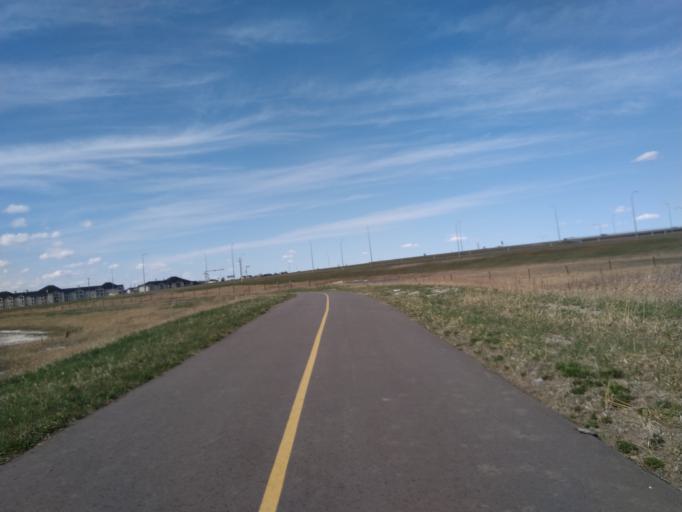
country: CA
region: Alberta
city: Chestermere
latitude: 51.0350
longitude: -113.9238
